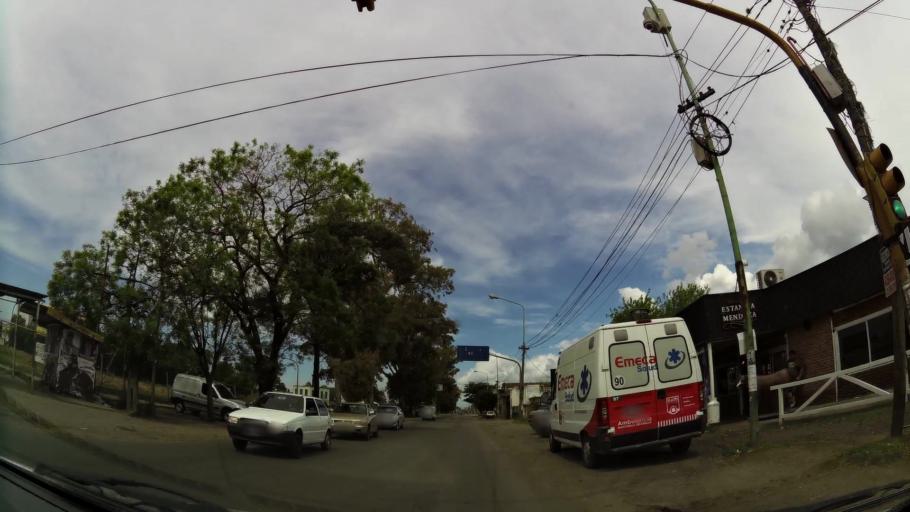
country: AR
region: Buenos Aires
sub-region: Partido de Quilmes
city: Quilmes
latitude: -34.7761
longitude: -58.2713
